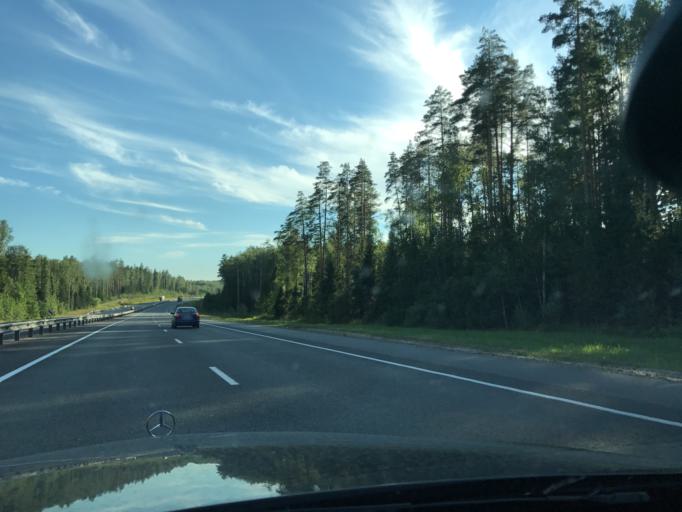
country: RU
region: Vladimir
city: Sudogda
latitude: 56.1513
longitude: 40.9182
